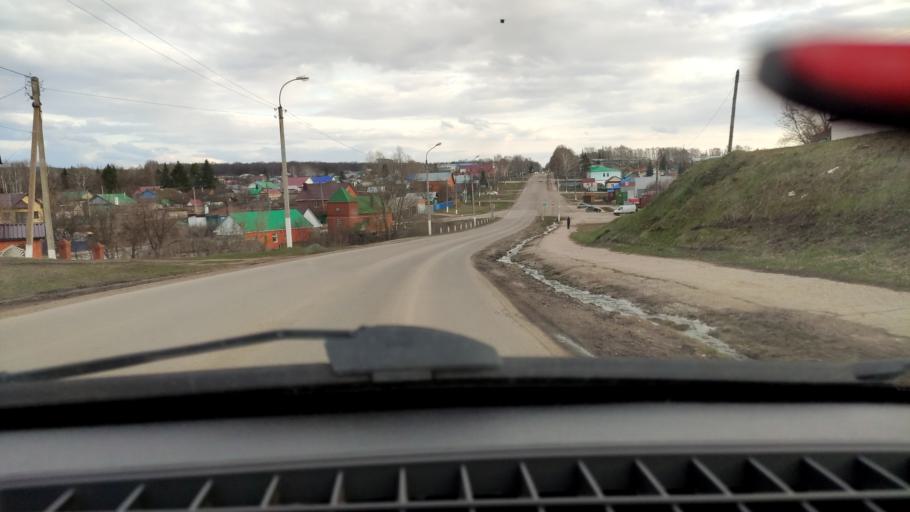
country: RU
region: Bashkortostan
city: Tolbazy
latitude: 54.0239
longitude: 55.8862
